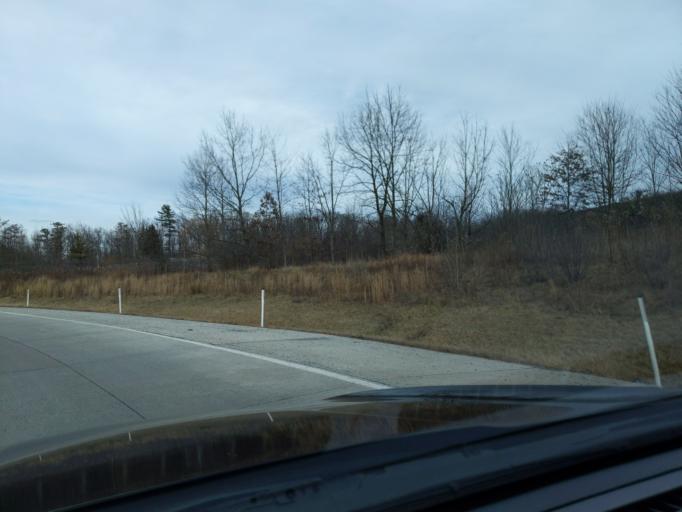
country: US
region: Pennsylvania
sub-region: Blair County
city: Lakemont
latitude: 40.4796
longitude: -78.3911
